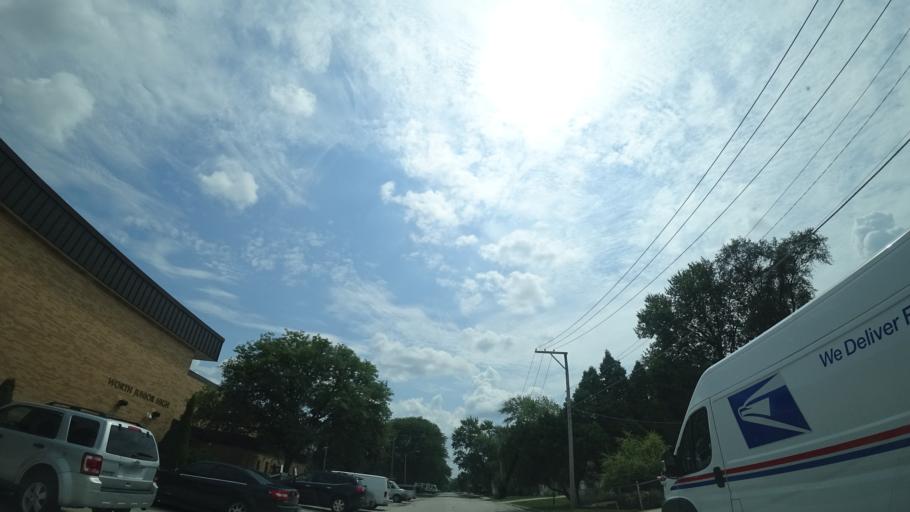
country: US
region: Illinois
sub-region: Cook County
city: Worth
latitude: 41.6890
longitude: -87.7915
